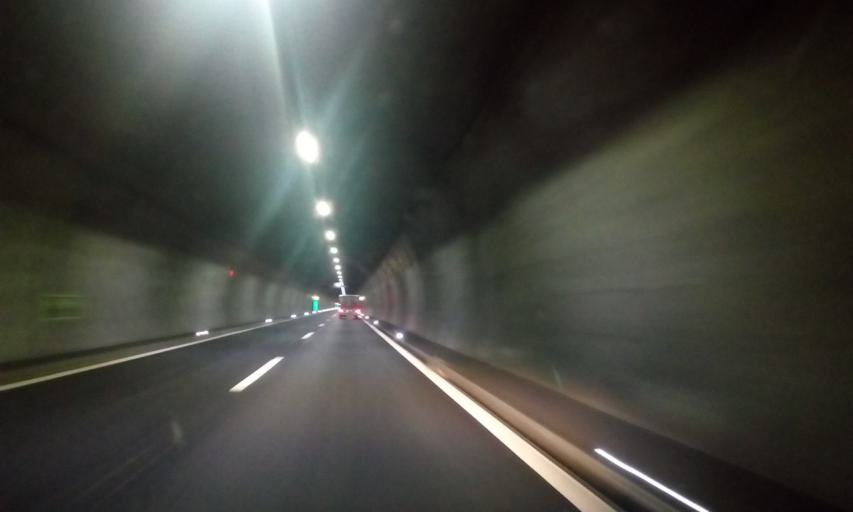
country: CH
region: Fribourg
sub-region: See District
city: Gurwolf
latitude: 46.9123
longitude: 7.1128
